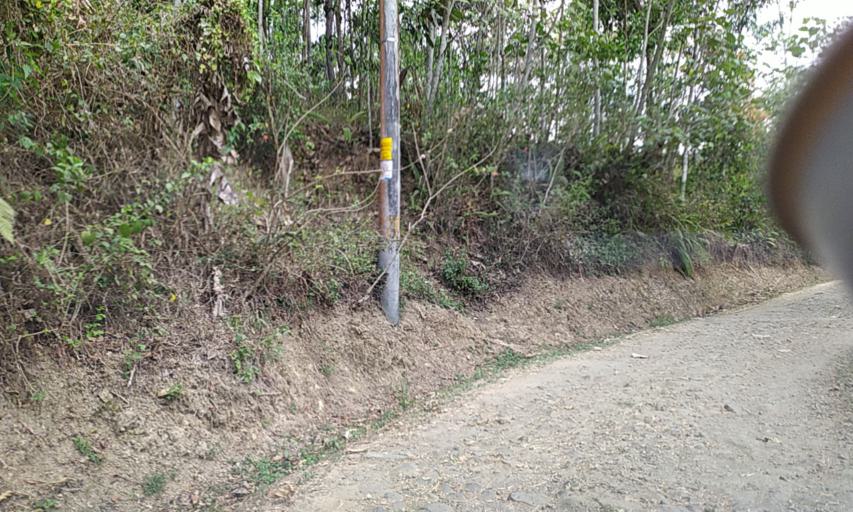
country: ID
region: Central Java
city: Jambuluwuk
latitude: -7.3289
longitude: 108.9463
